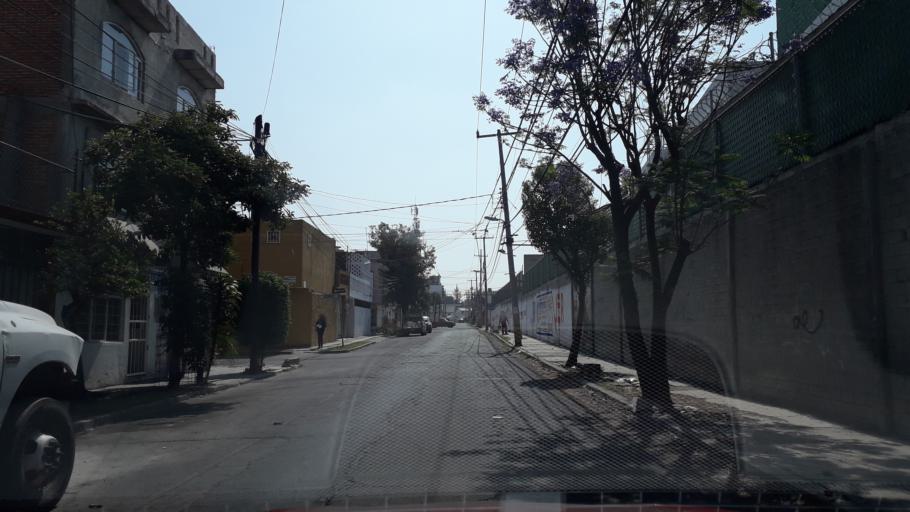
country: MX
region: Puebla
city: Puebla
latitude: 19.0767
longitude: -98.2137
